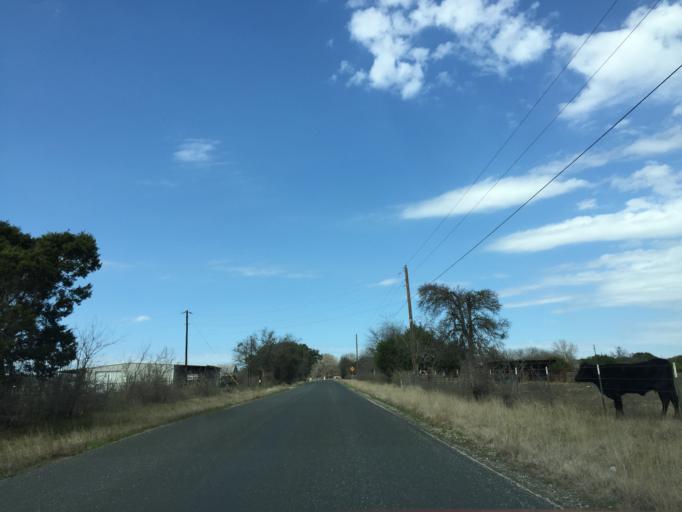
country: US
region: Texas
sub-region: Burnet County
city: Bertram
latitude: 30.7457
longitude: -97.9399
